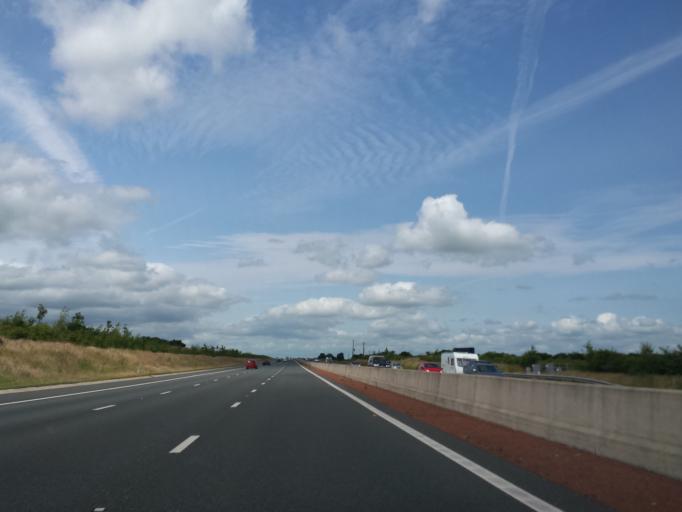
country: GB
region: England
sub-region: North Yorkshire
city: Bedale
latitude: 54.2556
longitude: -1.5117
